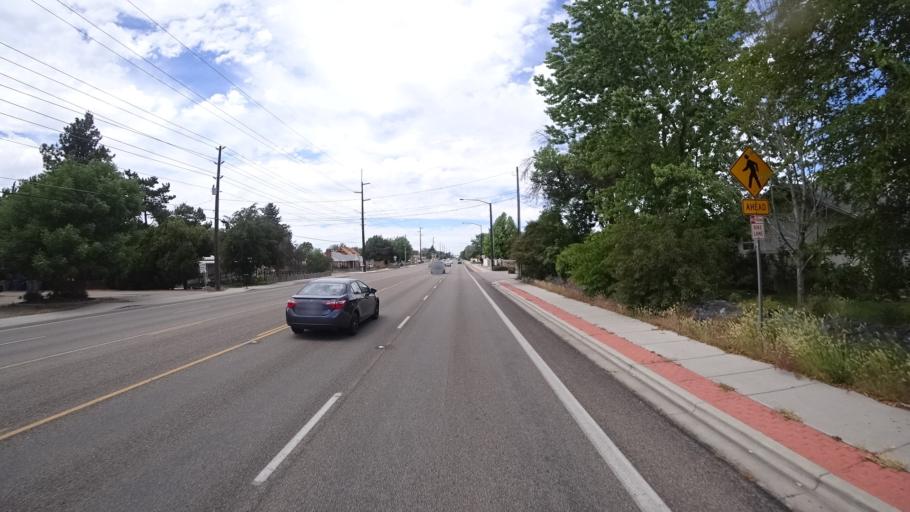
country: US
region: Idaho
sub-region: Ada County
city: Garden City
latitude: 43.6340
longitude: -116.2983
